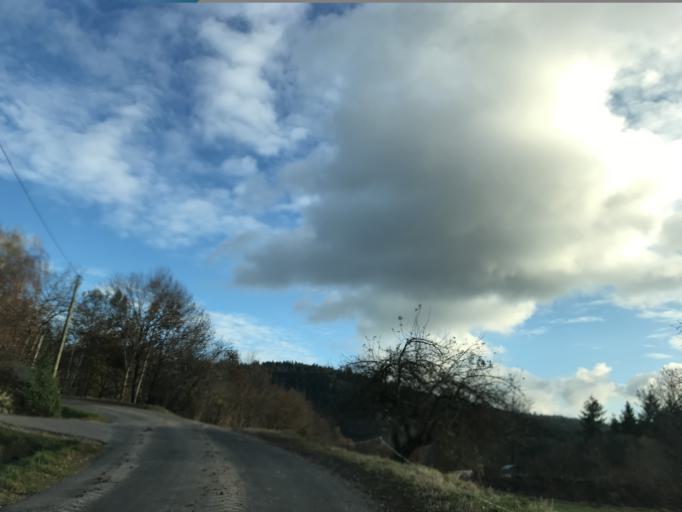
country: FR
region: Auvergne
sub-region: Departement du Puy-de-Dome
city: Celles-sur-Durolle
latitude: 45.7719
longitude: 3.6594
